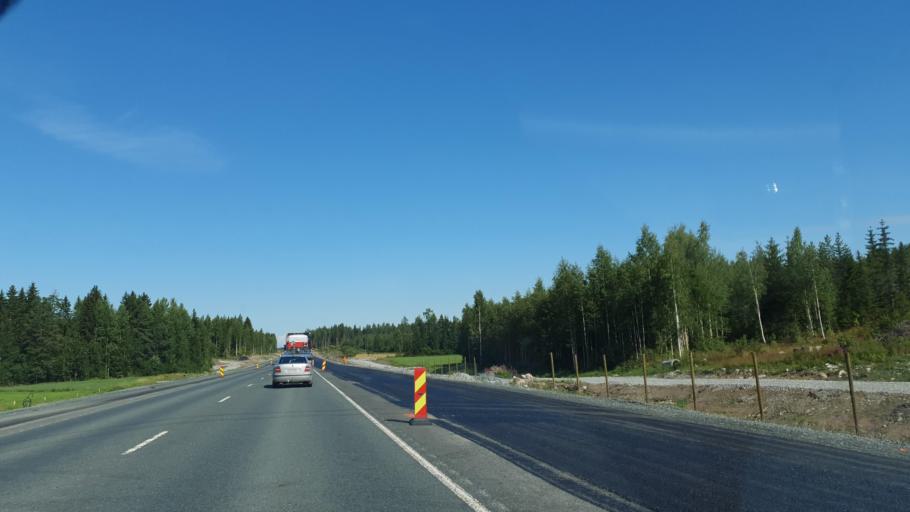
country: FI
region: Northern Savo
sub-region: Ylae-Savo
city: Lapinlahti
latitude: 63.2967
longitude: 27.4527
